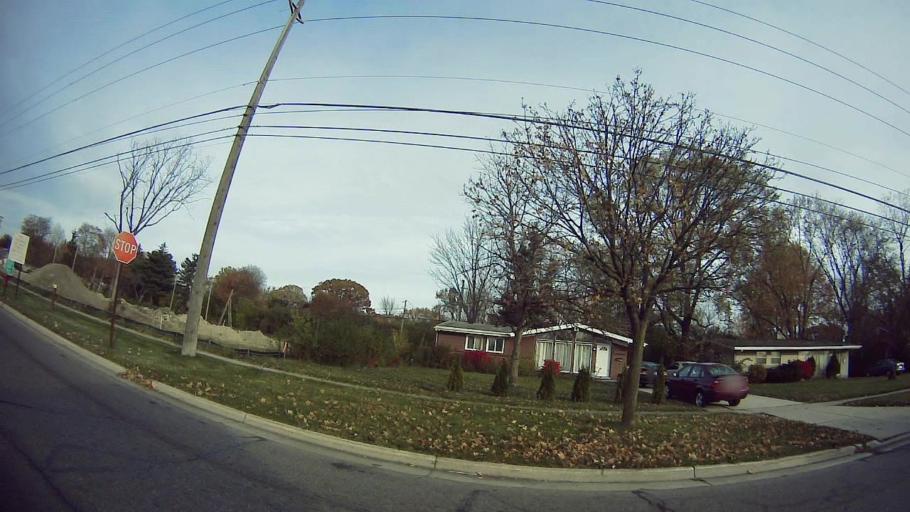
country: US
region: Michigan
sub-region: Oakland County
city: Lathrup Village
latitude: 42.4882
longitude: -83.2171
